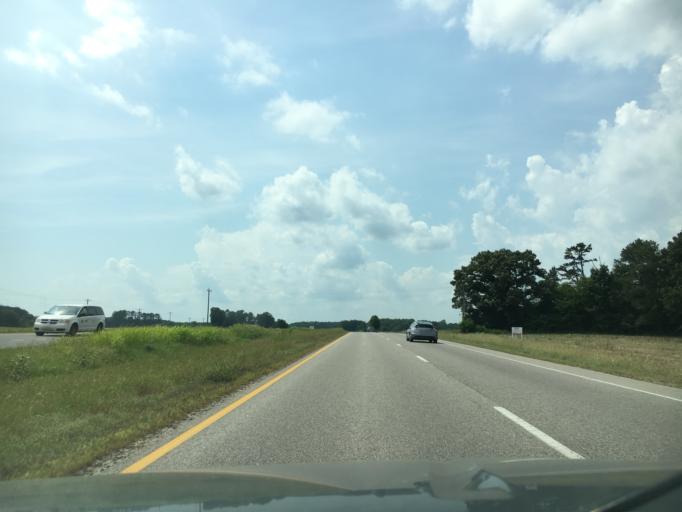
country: US
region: Virginia
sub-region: Amelia County
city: Amelia Court House
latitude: 37.3627
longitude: -77.8938
